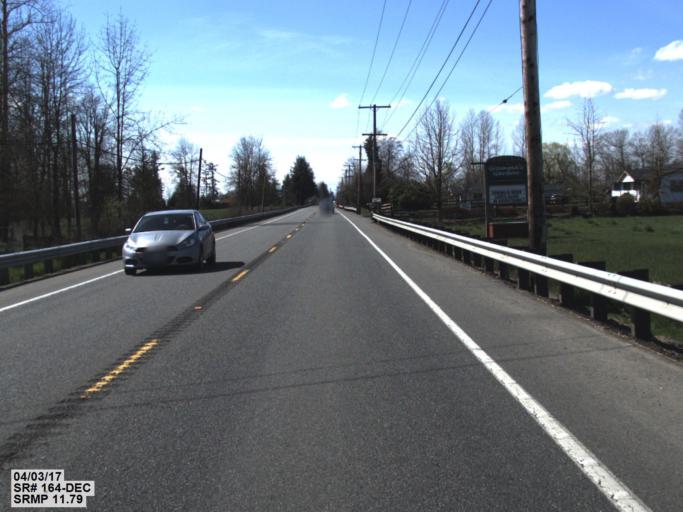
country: US
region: Washington
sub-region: Pierce County
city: Buckley
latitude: 47.2102
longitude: -122.0470
